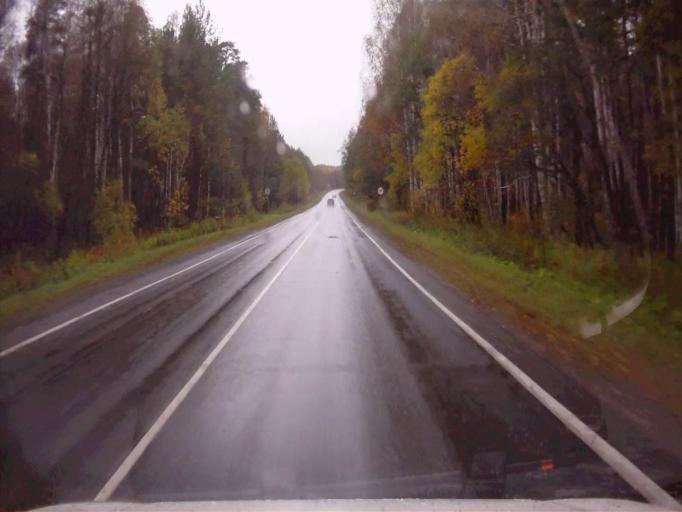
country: RU
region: Chelyabinsk
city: Verkhniy Ufaley
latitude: 55.9697
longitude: 60.3652
